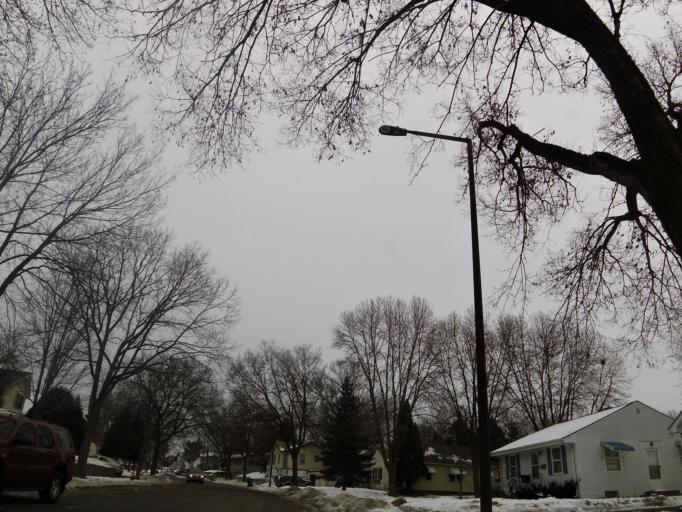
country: US
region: Minnesota
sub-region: Ramsey County
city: Maplewood
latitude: 44.9664
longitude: -93.0147
